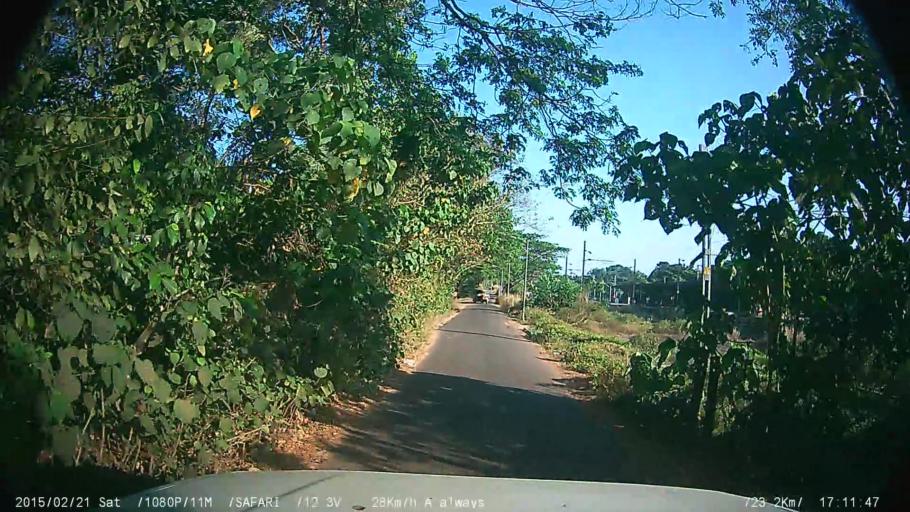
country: IN
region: Kerala
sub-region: Kottayam
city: Changanacheri
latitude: 9.4500
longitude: 76.5484
